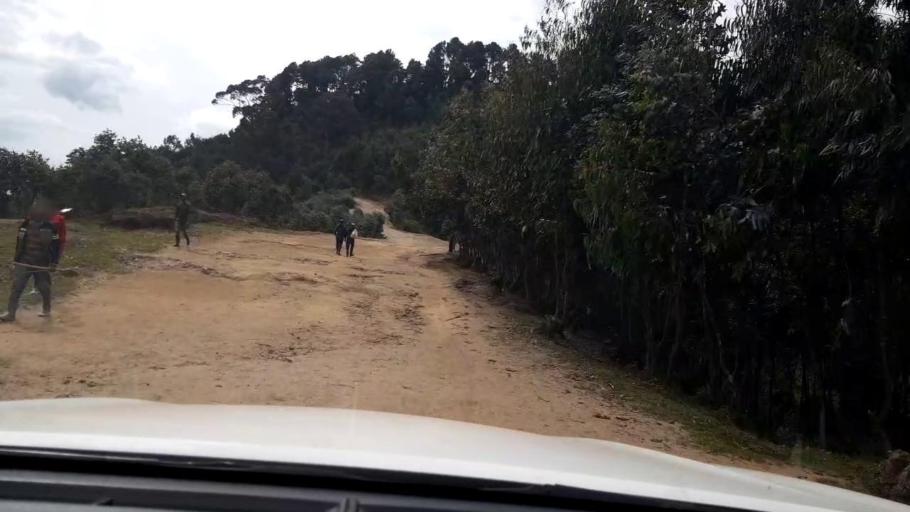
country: RW
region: Western Province
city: Kibuye
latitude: -1.8783
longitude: 29.4553
